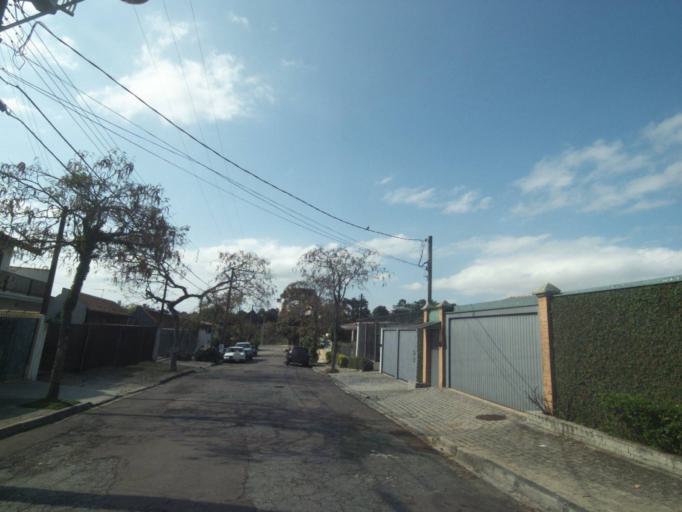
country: BR
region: Parana
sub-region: Pinhais
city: Pinhais
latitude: -25.4039
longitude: -49.2129
